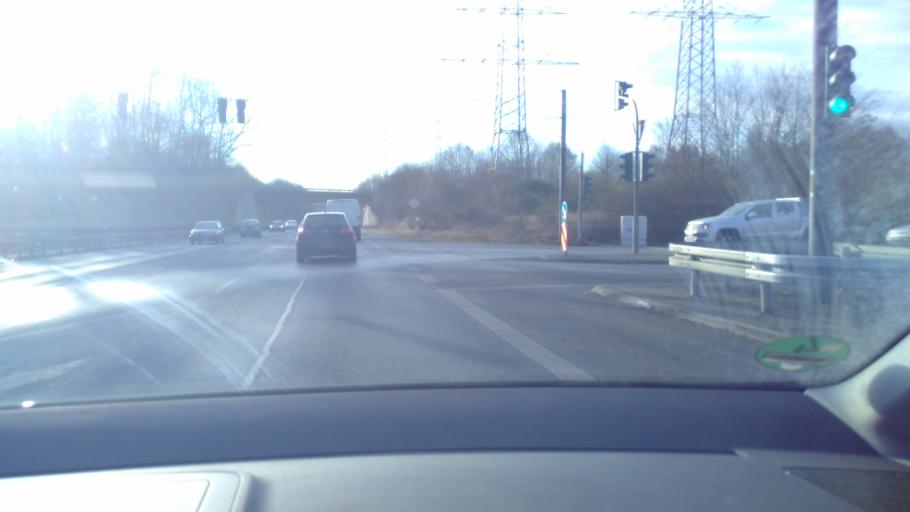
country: DE
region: North Rhine-Westphalia
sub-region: Regierungsbezirk Koln
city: Bergheim
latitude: 50.9678
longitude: 6.6337
